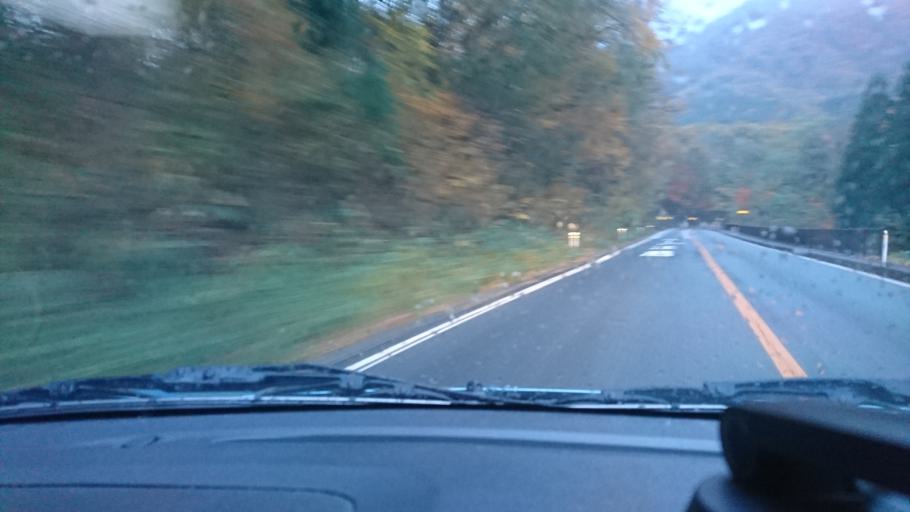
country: JP
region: Miyagi
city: Furukawa
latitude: 38.7329
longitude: 140.6881
